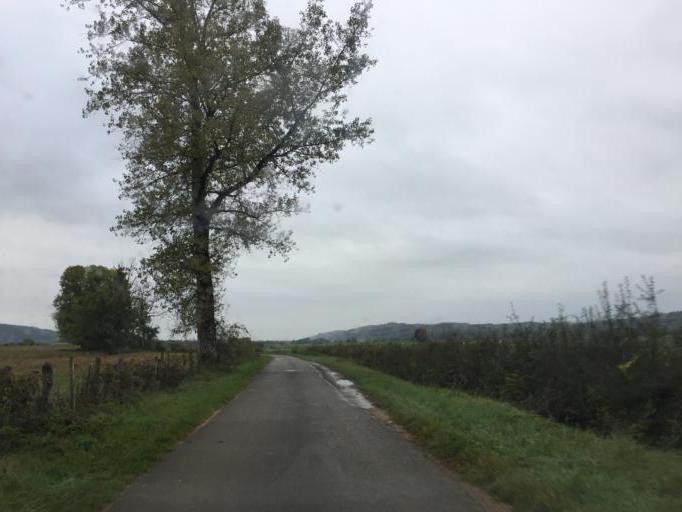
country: FR
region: Franche-Comte
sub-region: Departement du Jura
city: Orgelet
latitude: 46.5251
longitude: 5.5617
